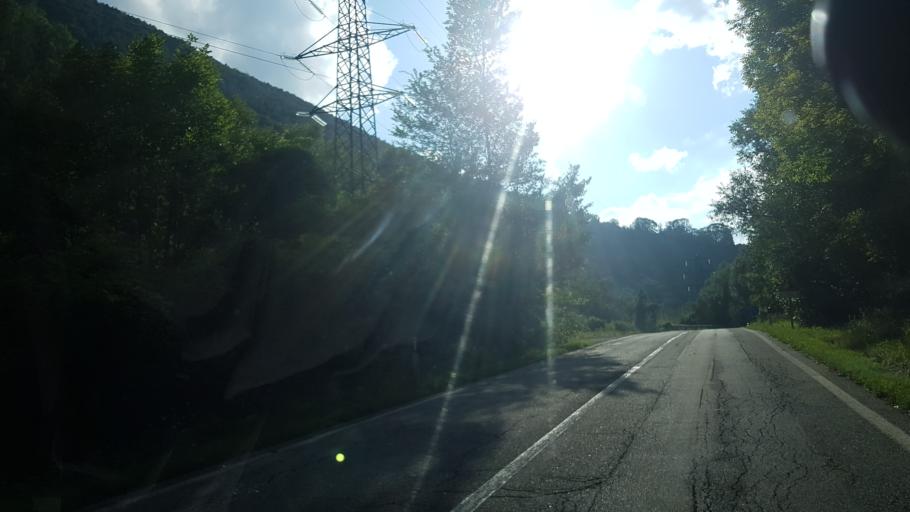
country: IT
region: Piedmont
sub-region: Provincia di Cuneo
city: Sampeyre
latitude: 44.5727
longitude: 7.2270
